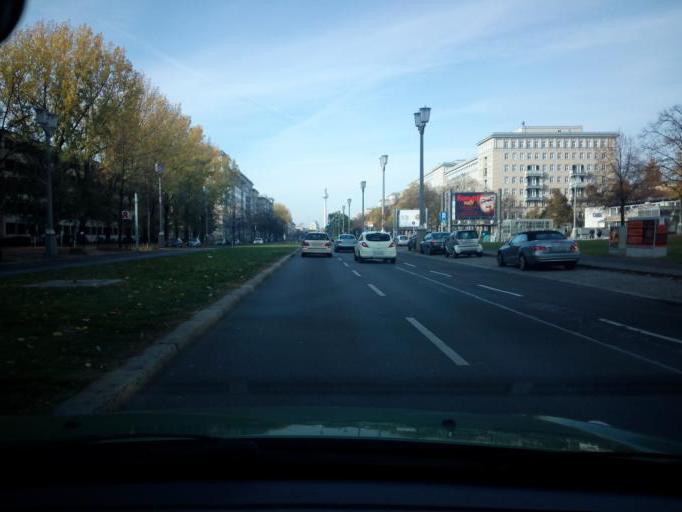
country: DE
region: Berlin
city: Friedrichshain Bezirk
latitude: 52.5161
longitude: 13.4515
